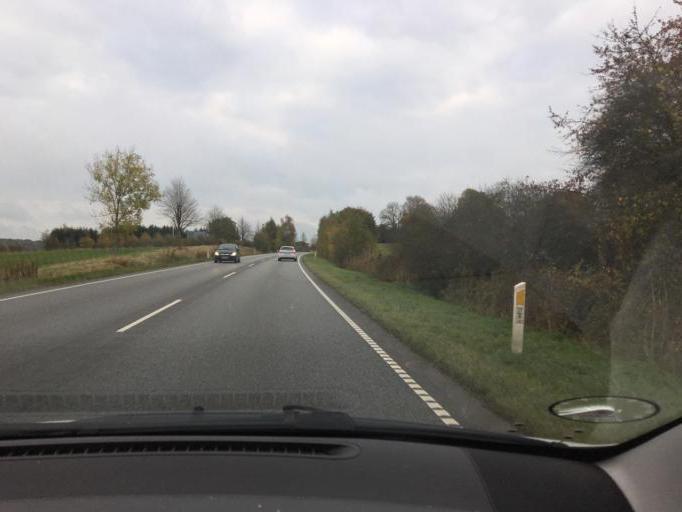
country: DK
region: South Denmark
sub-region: Fredericia Kommune
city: Fredericia
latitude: 55.6186
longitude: 9.7455
